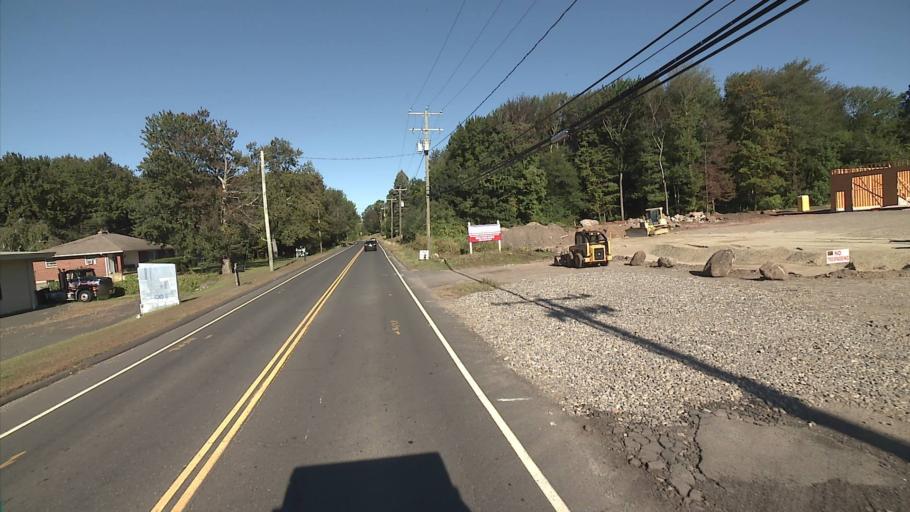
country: US
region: Connecticut
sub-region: New Haven County
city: Prospect
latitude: 41.5050
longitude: -72.9852
